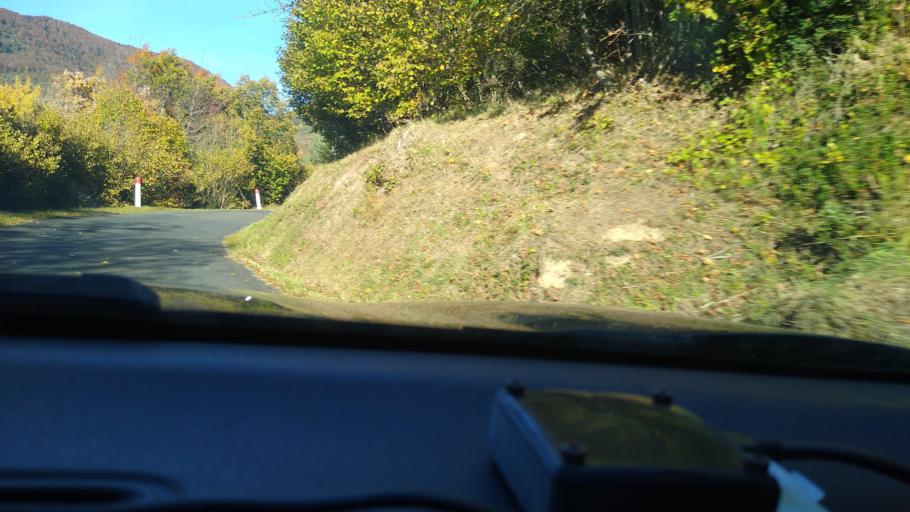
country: FR
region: Languedoc-Roussillon
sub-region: Departement de l'Aude
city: Quillan
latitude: 42.7357
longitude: 2.1367
